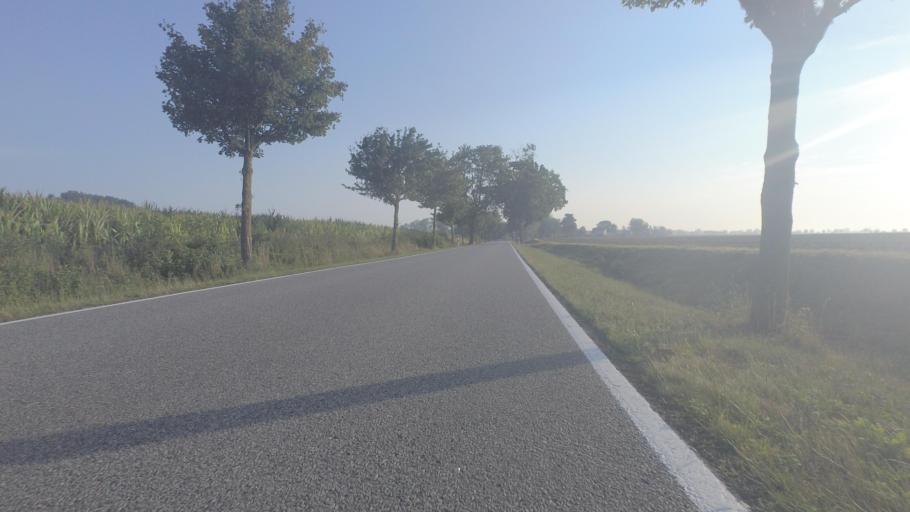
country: DE
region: Mecklenburg-Vorpommern
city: Demmin
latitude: 53.9263
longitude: 13.0798
